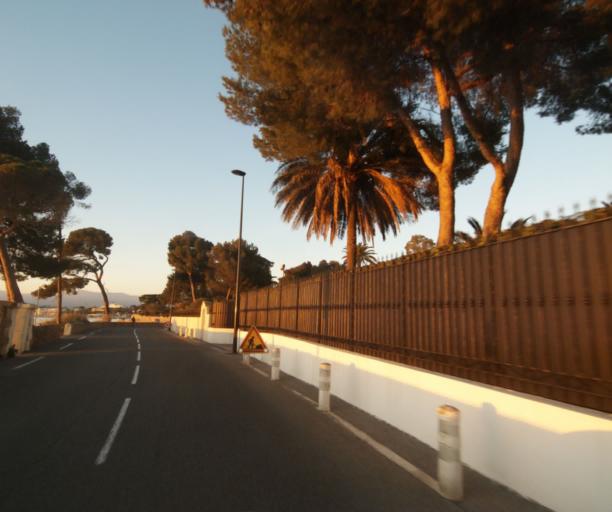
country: FR
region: Provence-Alpes-Cote d'Azur
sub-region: Departement des Alpes-Maritimes
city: Antibes
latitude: 43.5528
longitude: 7.1223
